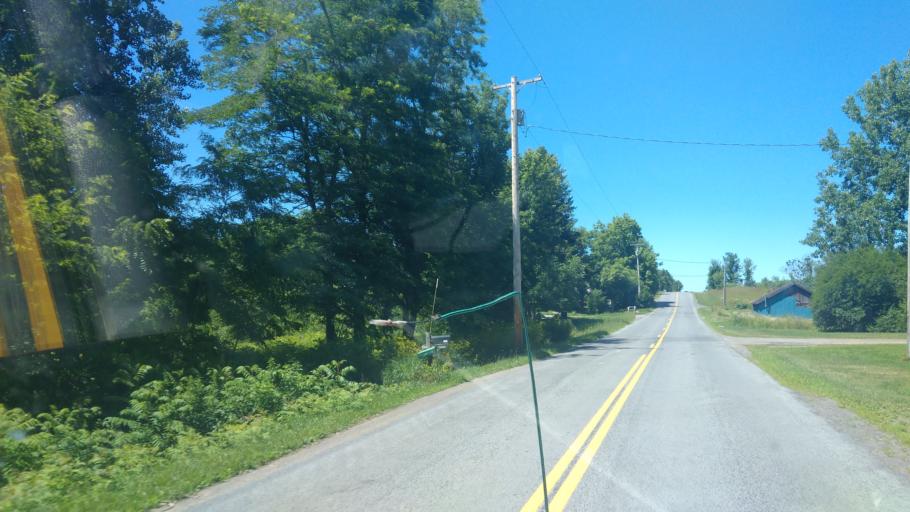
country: US
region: New York
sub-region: Wayne County
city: Lyons
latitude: 43.1505
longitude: -76.9788
